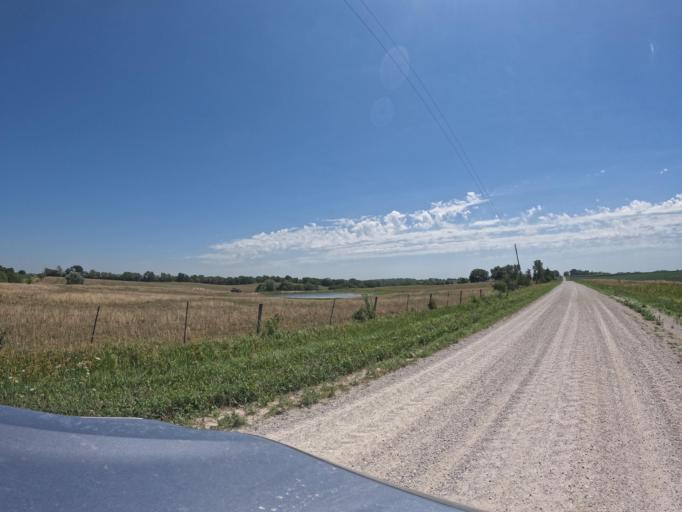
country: US
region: Iowa
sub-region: Keokuk County
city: Sigourney
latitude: 41.4233
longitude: -92.3163
